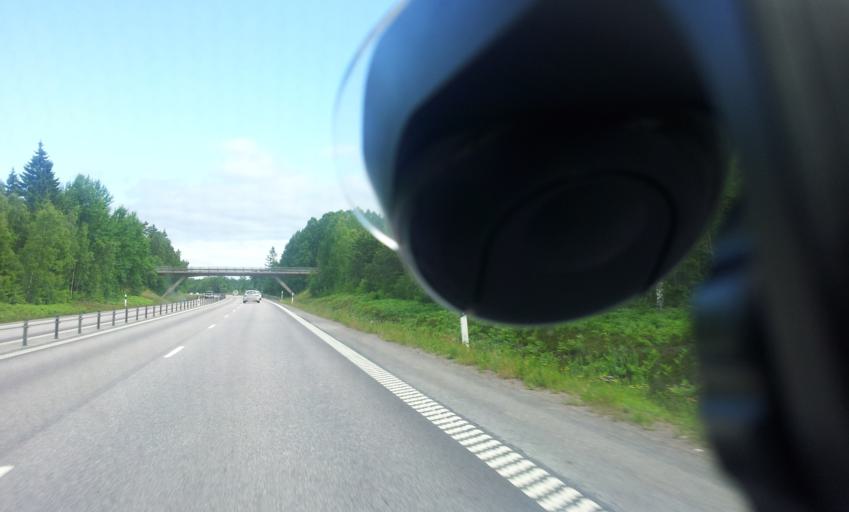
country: SE
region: Kalmar
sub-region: Kalmar Kommun
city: Lindsdal
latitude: 56.7245
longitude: 16.3159
